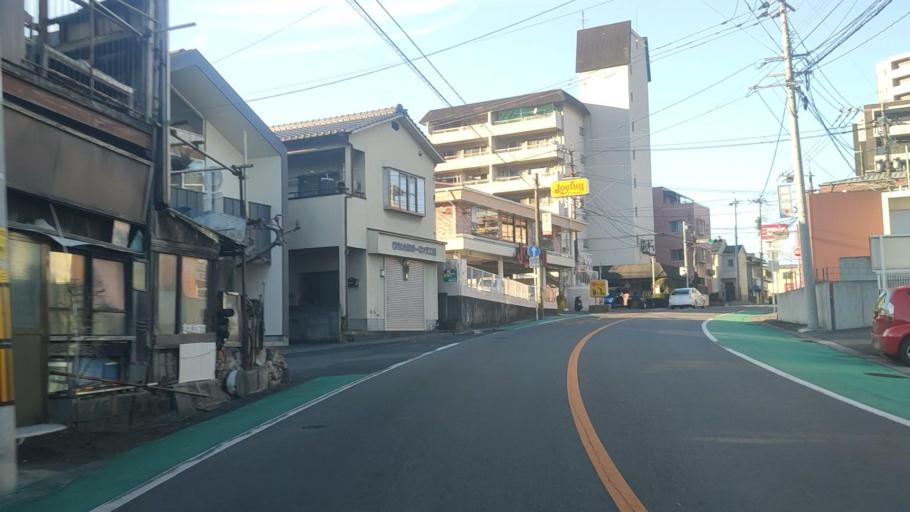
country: JP
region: Oita
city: Beppu
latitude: 33.2779
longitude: 131.4895
